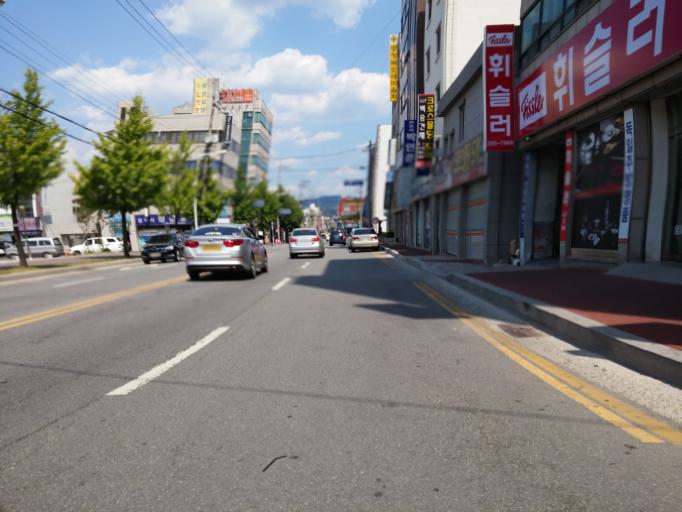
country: KR
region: Chungcheongbuk-do
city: Cheongju-si
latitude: 36.6183
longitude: 127.4847
